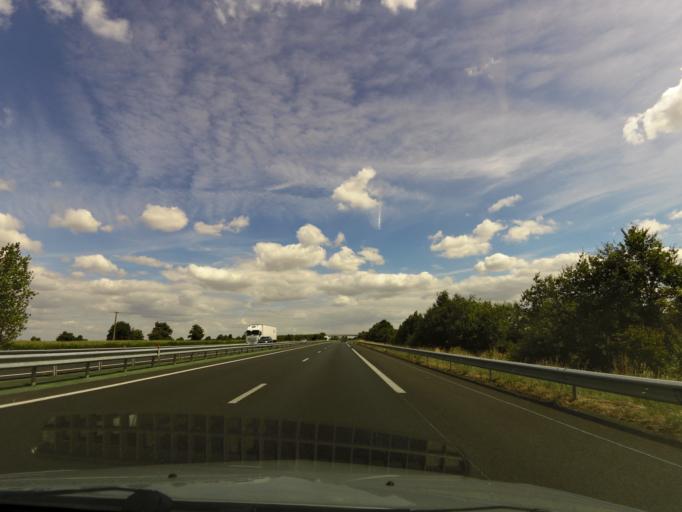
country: FR
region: Pays de la Loire
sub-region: Departement de la Vendee
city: Chauche
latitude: 46.8434
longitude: -1.2517
